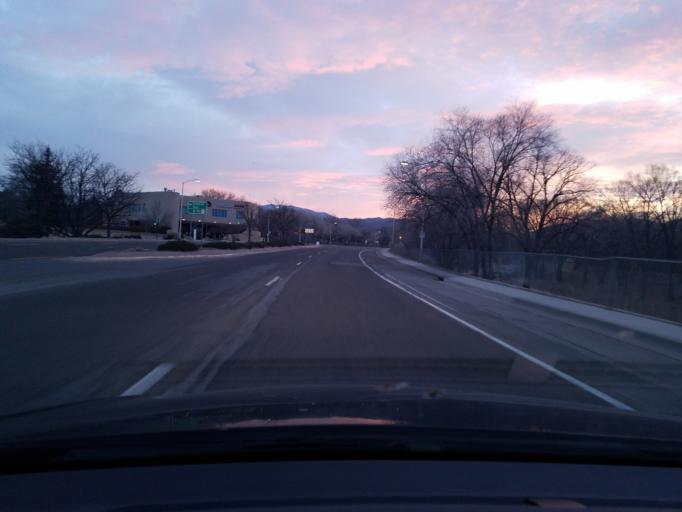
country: US
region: New Mexico
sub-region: Santa Fe County
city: Santa Fe
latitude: 35.6918
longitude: -105.9493
